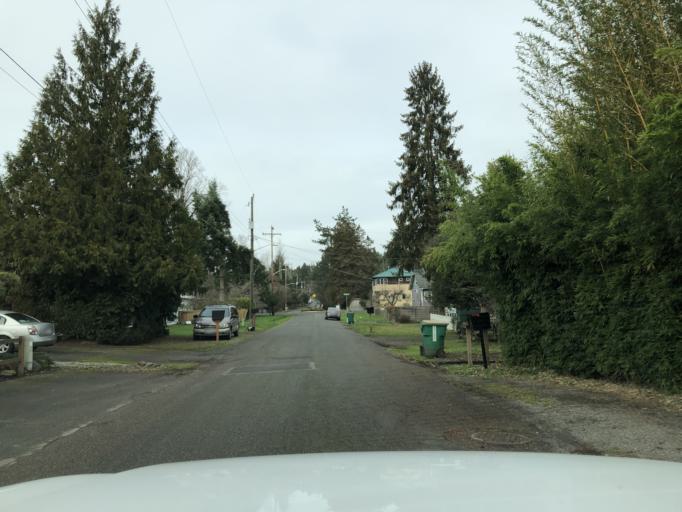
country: US
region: Washington
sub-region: King County
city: Lake Forest Park
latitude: 47.7038
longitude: -122.2868
